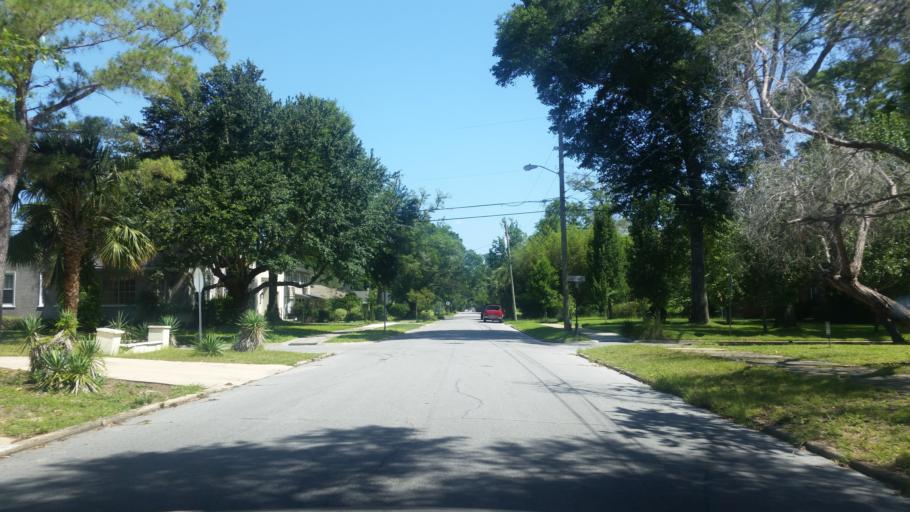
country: US
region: Florida
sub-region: Escambia County
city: Pensacola
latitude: 30.4263
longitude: -87.2213
